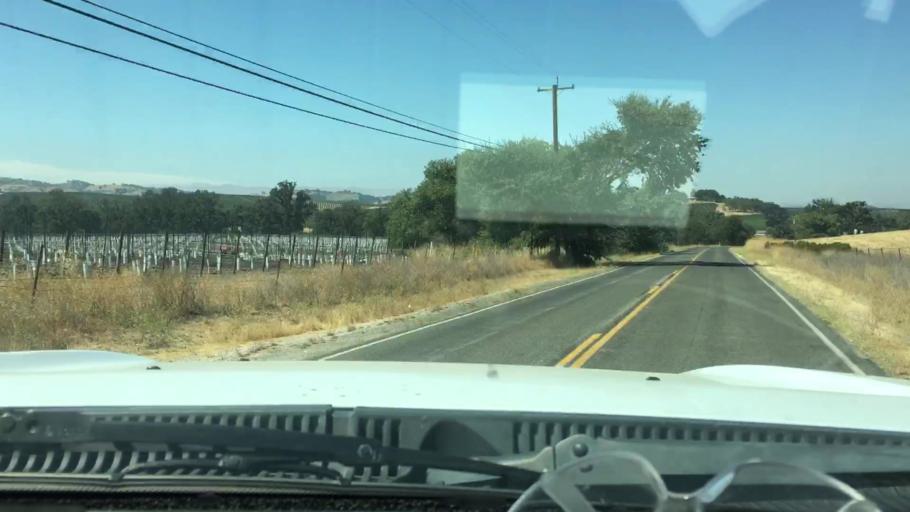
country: US
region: California
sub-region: San Luis Obispo County
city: Paso Robles
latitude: 35.6036
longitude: -120.6468
